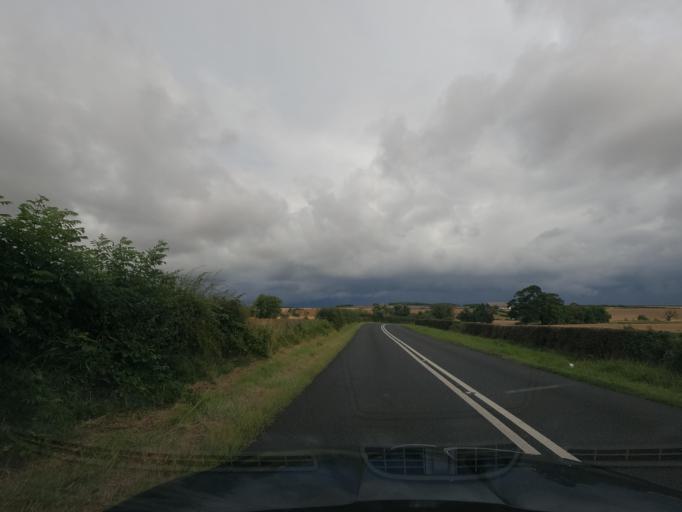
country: GB
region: England
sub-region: Northumberland
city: Ancroft
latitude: 55.7049
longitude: -1.9994
